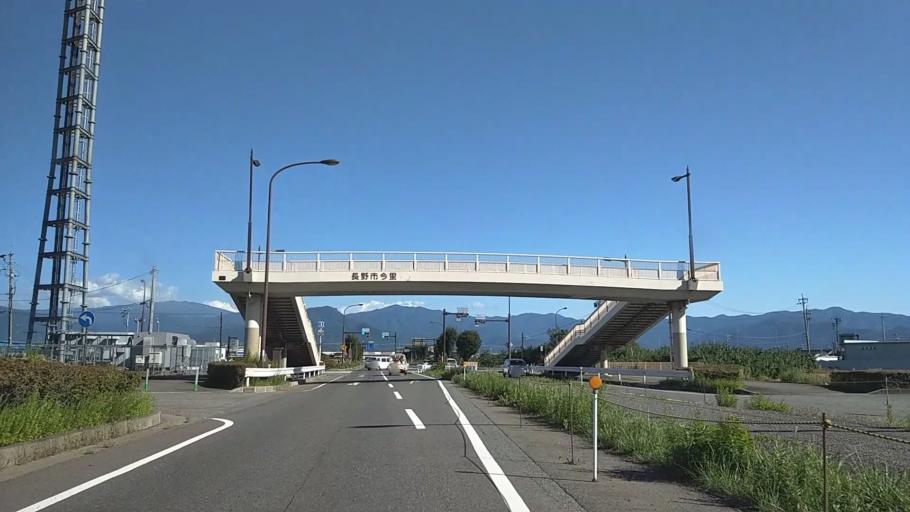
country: JP
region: Nagano
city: Nagano-shi
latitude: 36.6120
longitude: 138.1432
